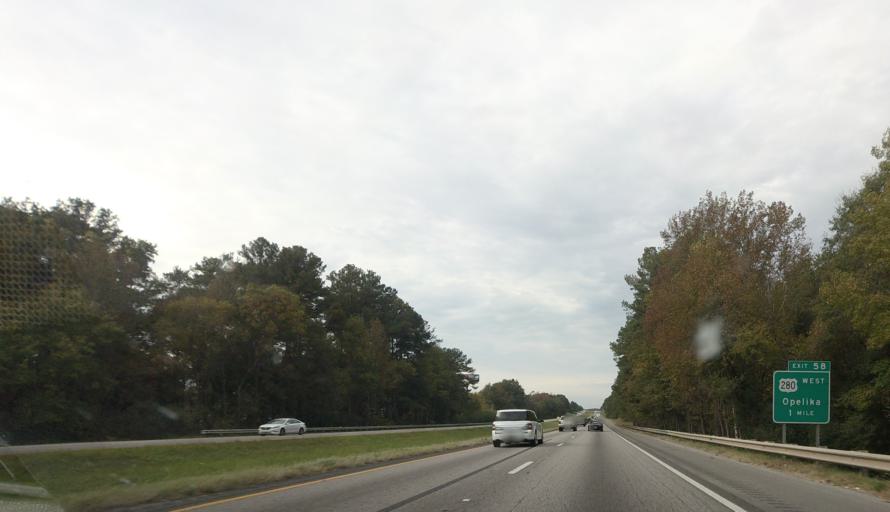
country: US
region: Alabama
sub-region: Lee County
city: Opelika
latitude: 32.6277
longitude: -85.3805
